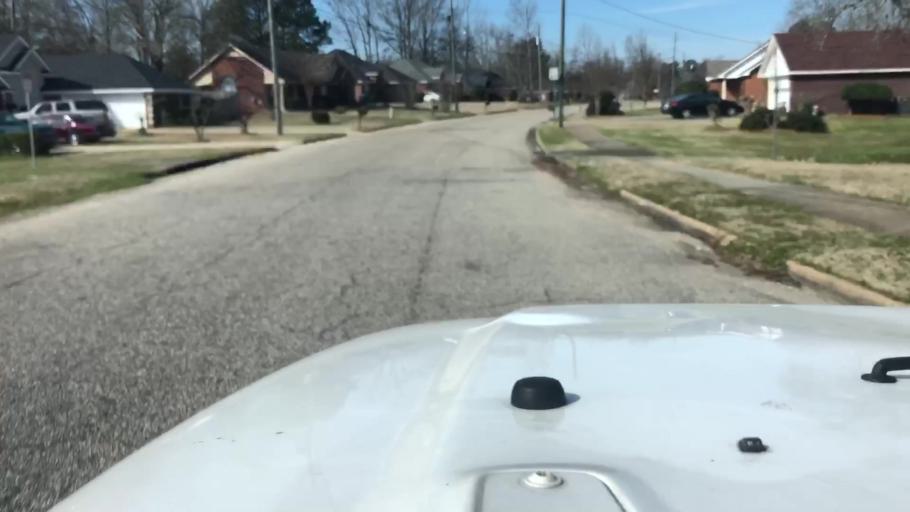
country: US
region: Alabama
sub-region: Elmore County
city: Blue Ridge
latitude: 32.4079
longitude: -86.1935
